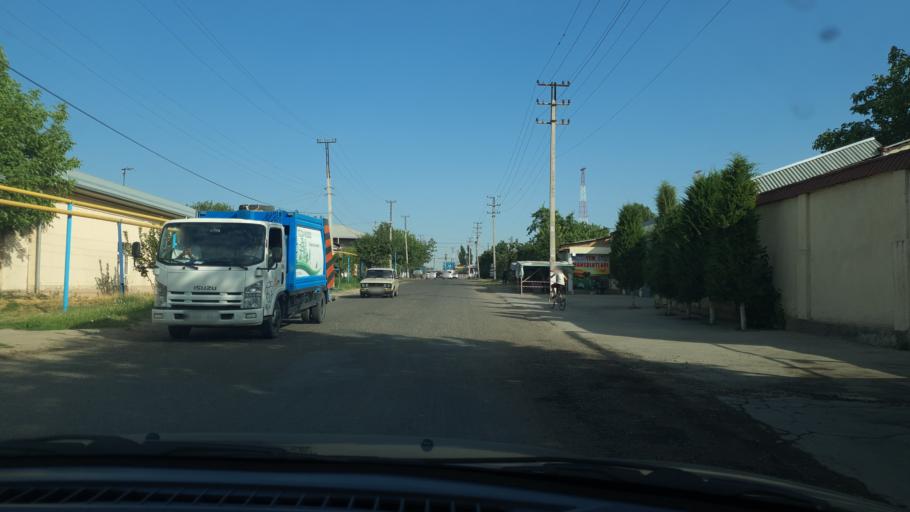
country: UZ
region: Toshkent
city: Urtaowul
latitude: 41.2062
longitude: 69.1495
